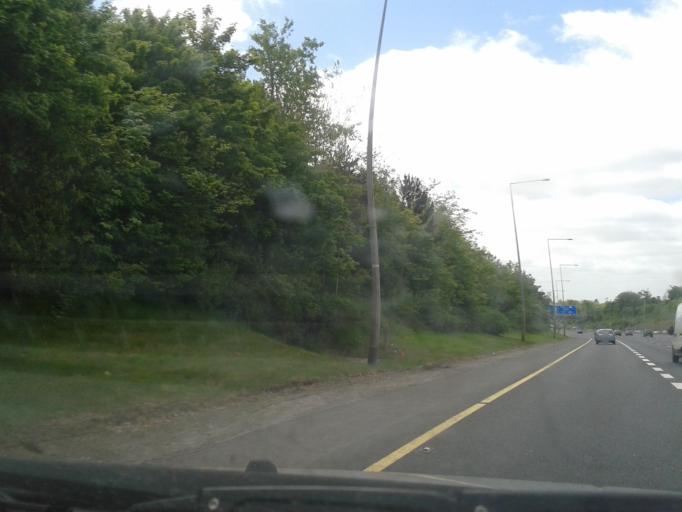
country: IE
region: Leinster
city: Castleknock
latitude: 53.3891
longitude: -6.3522
